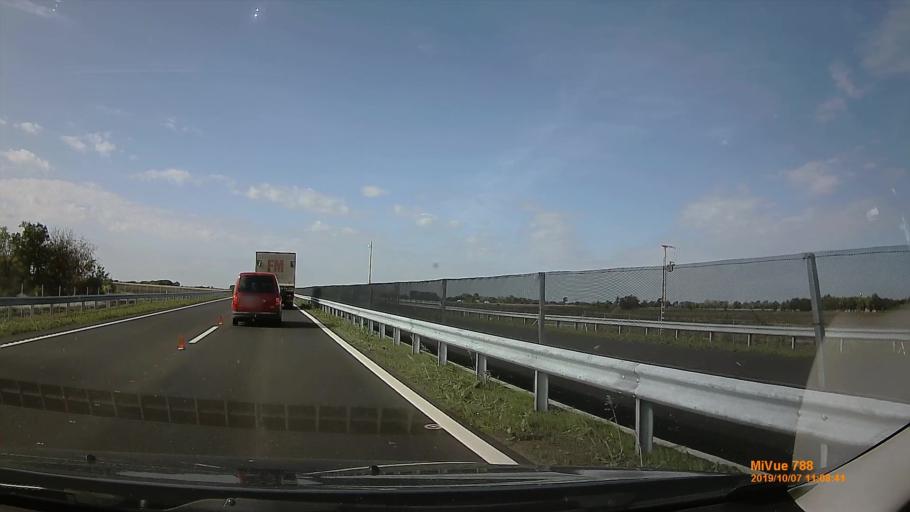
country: HU
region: Bekes
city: Kondoros
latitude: 46.7455
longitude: 20.8447
